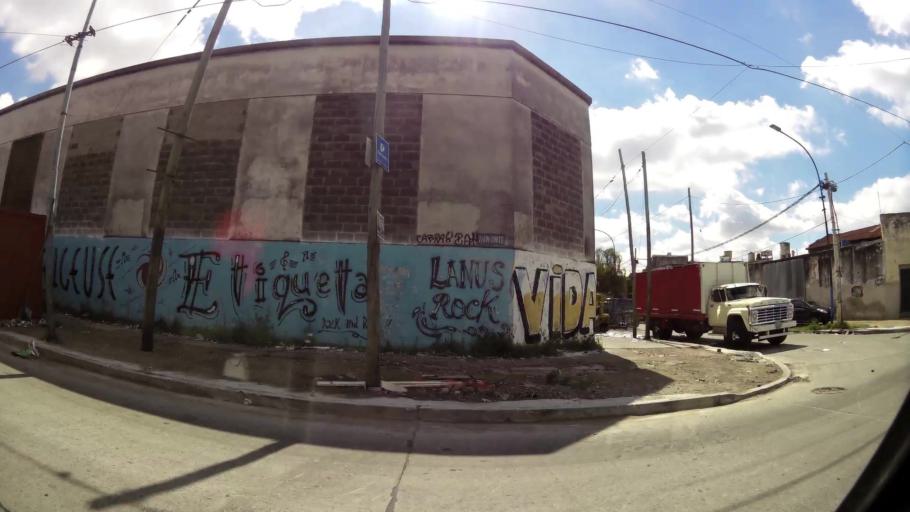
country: AR
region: Buenos Aires
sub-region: Partido de Lanus
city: Lanus
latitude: -34.6852
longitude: -58.4182
